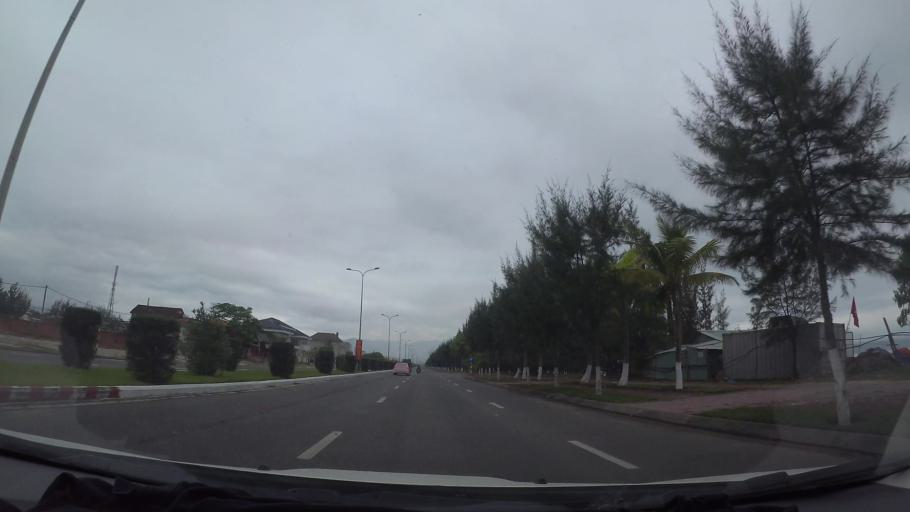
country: VN
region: Da Nang
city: Lien Chieu
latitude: 16.0993
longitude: 108.1418
